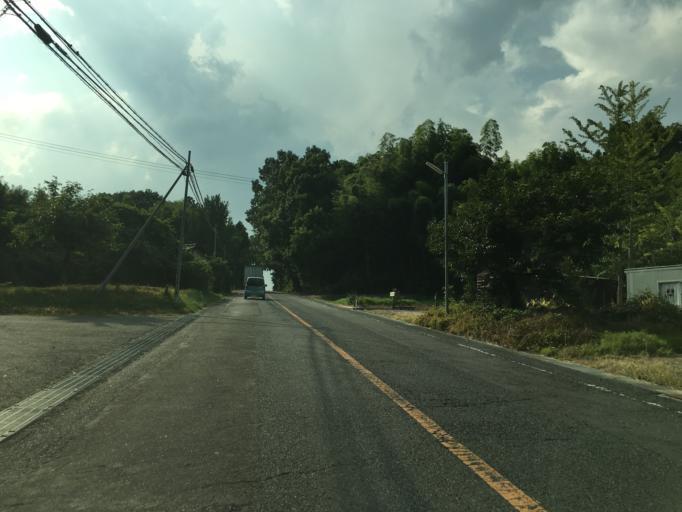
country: JP
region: Fukushima
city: Motomiya
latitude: 37.4684
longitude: 140.4222
